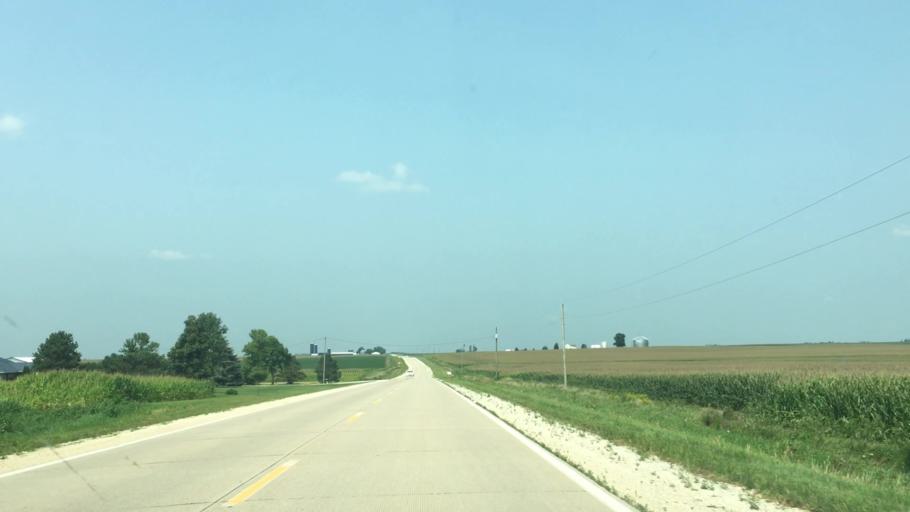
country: US
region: Iowa
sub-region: Fayette County
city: Fayette
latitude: 42.7268
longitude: -91.8042
